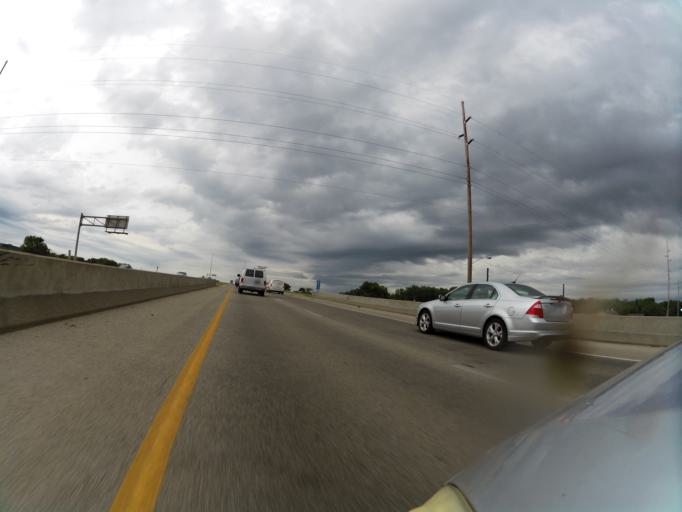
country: US
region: Kansas
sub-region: Sedgwick County
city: Bellaire
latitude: 37.7435
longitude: -97.2994
